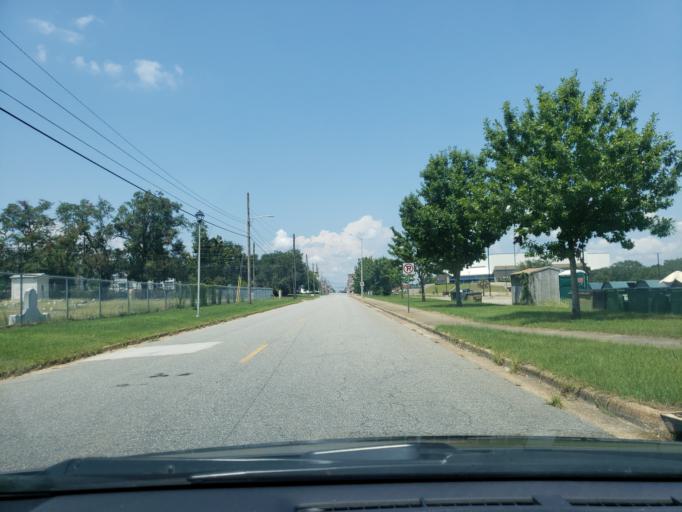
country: US
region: Georgia
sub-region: Dougherty County
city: Albany
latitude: 31.5706
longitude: -84.1514
